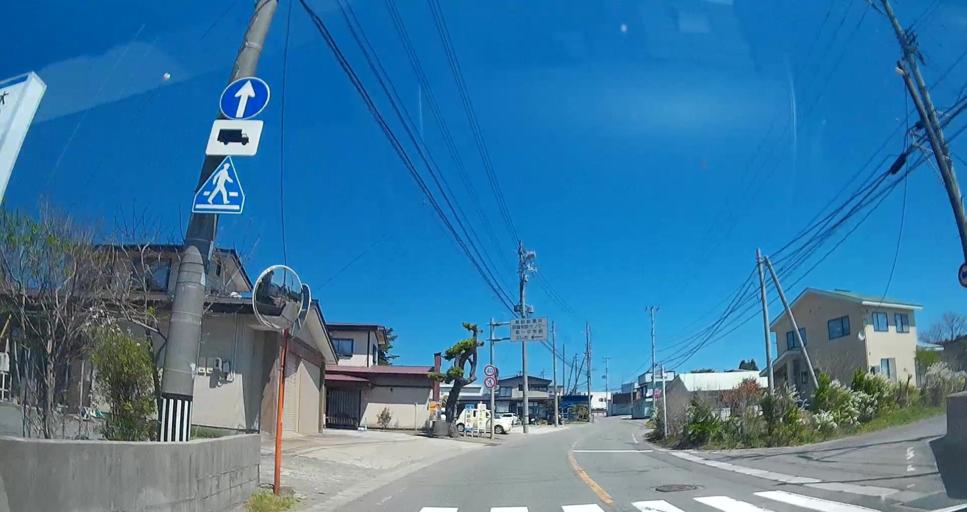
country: JP
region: Aomori
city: Misawa
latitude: 40.9623
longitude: 141.3737
